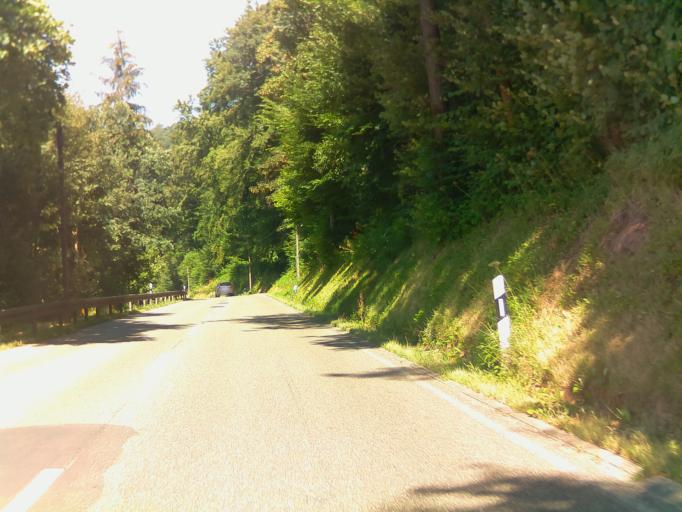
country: DE
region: Baden-Wuerttemberg
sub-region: Regierungsbezirk Stuttgart
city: Wertheim
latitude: 49.7377
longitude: 9.5233
